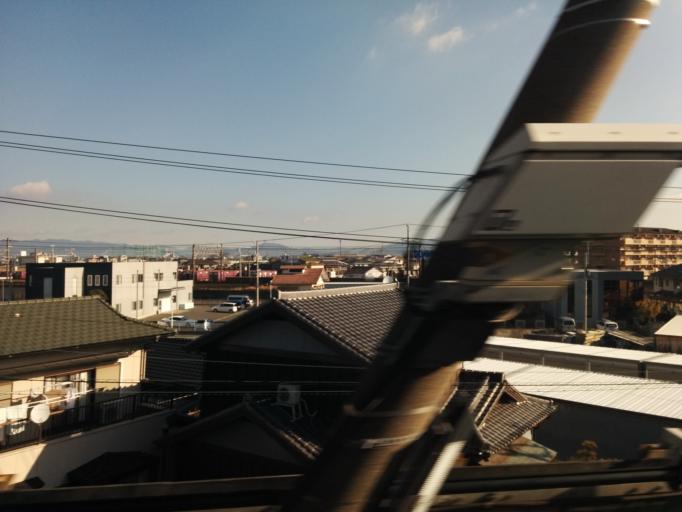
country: JP
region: Aichi
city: Toyohashi
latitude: 34.7753
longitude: 137.3726
